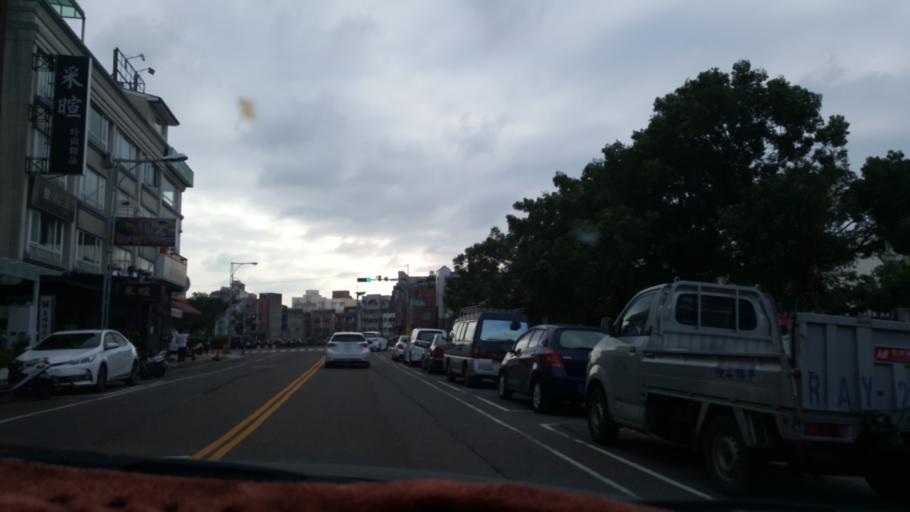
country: TW
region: Taiwan
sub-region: Hsinchu
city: Zhubei
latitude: 24.8327
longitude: 121.0099
